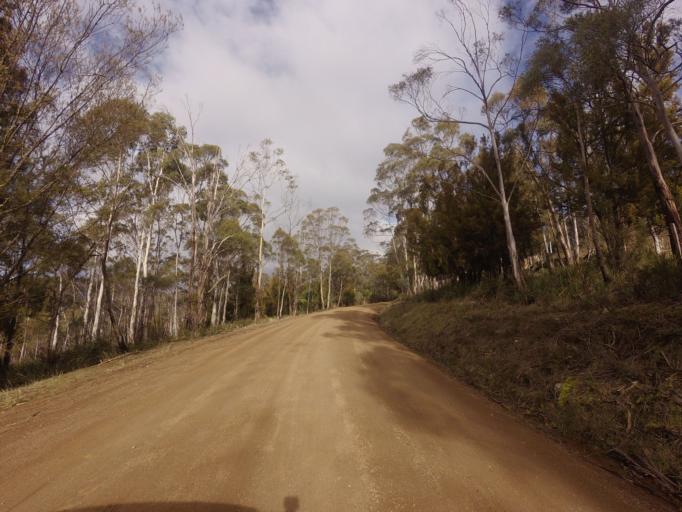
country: AU
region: Tasmania
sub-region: Derwent Valley
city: New Norfolk
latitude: -42.7864
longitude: 146.9382
